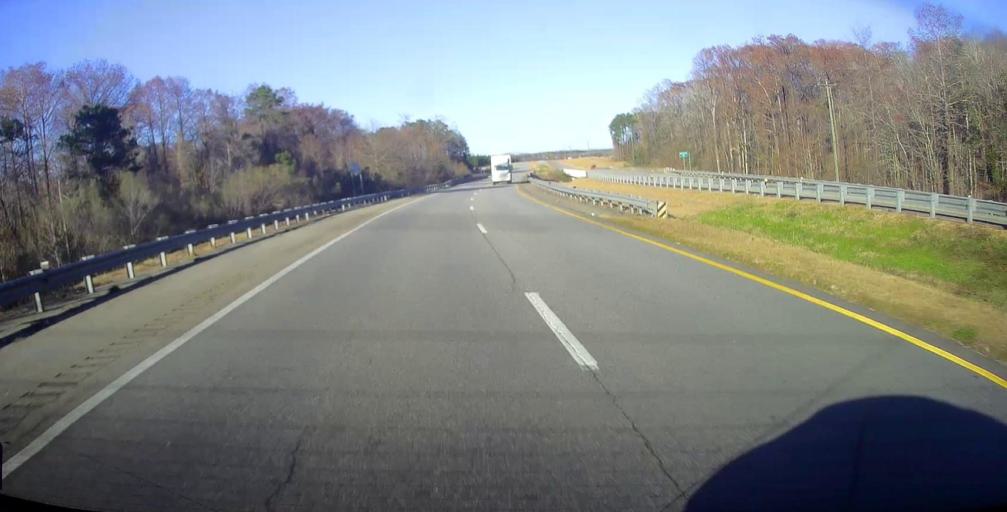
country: US
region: Georgia
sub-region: Sumter County
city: Americus
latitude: 31.9271
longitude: -84.2655
